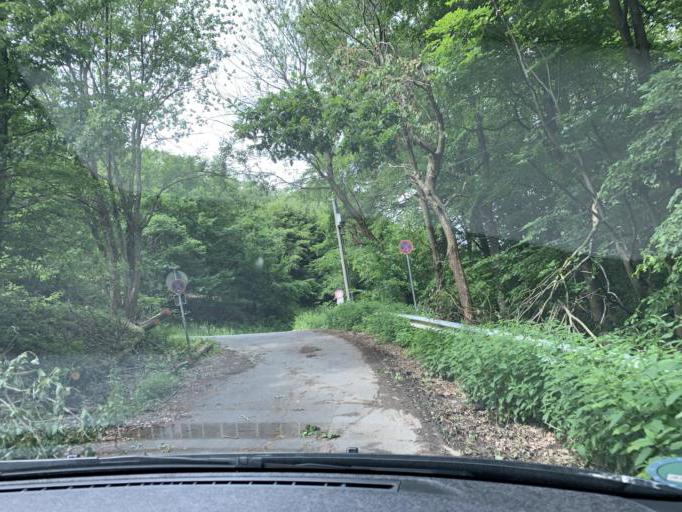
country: DE
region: North Rhine-Westphalia
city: Heimbach
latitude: 50.6484
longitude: 6.4138
